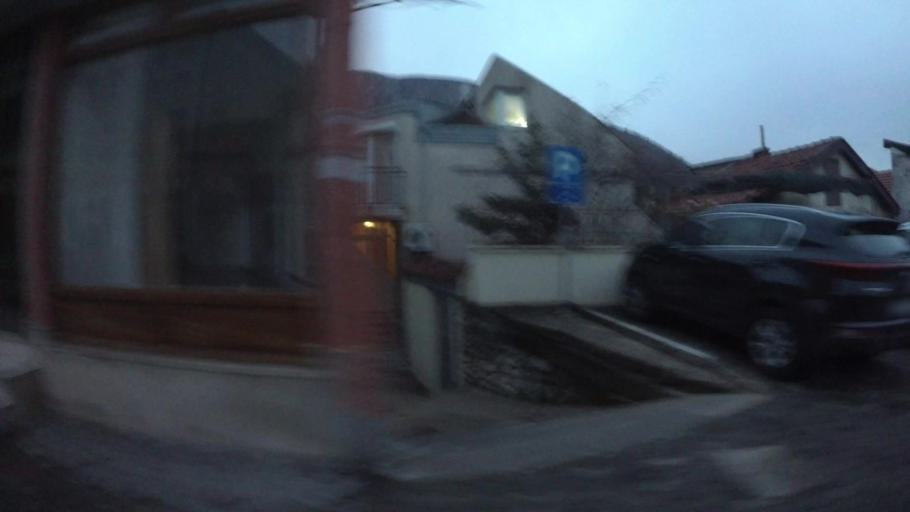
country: BA
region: Federation of Bosnia and Herzegovina
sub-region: Hercegovacko-Bosanski Kanton
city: Mostar
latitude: 43.3324
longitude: 17.8182
